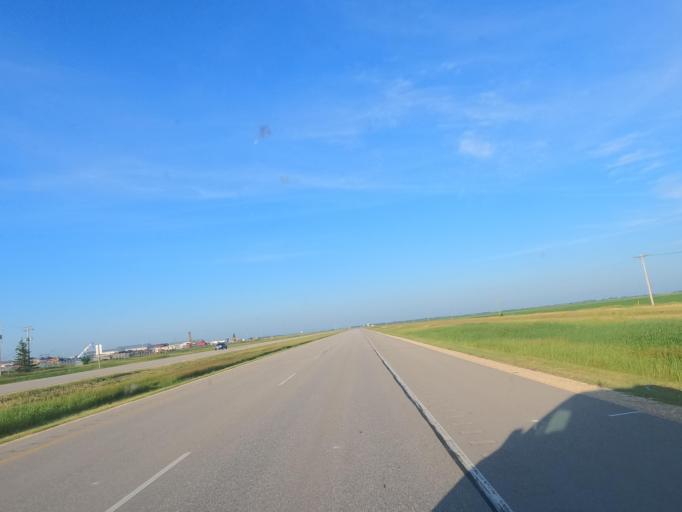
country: CA
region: Manitoba
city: Selkirk
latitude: 50.0589
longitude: -97.0511
